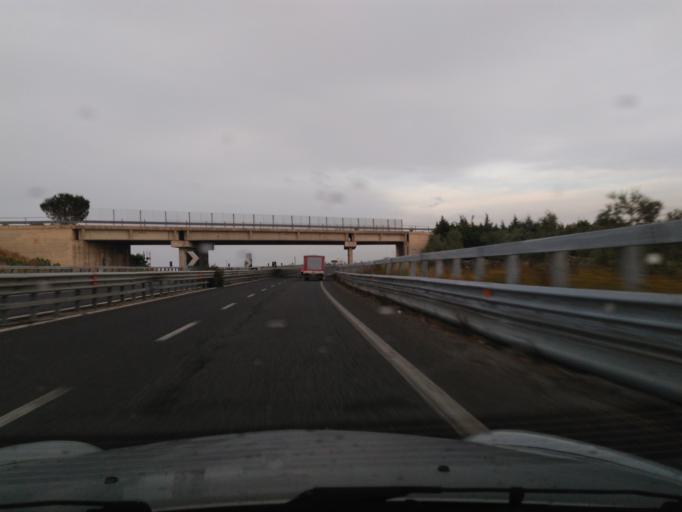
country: IT
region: Apulia
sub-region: Provincia di Bari
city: Giovinazzo
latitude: 41.1733
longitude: 16.6884
